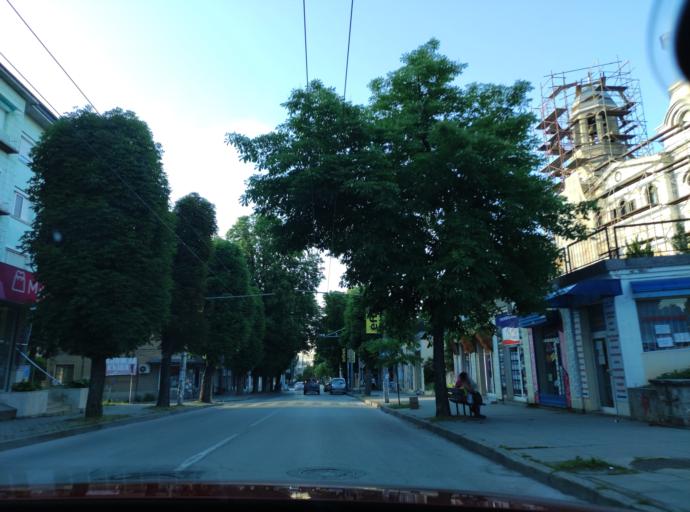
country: BG
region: Pleven
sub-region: Obshtina Pleven
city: Pleven
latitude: 43.4040
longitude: 24.6209
